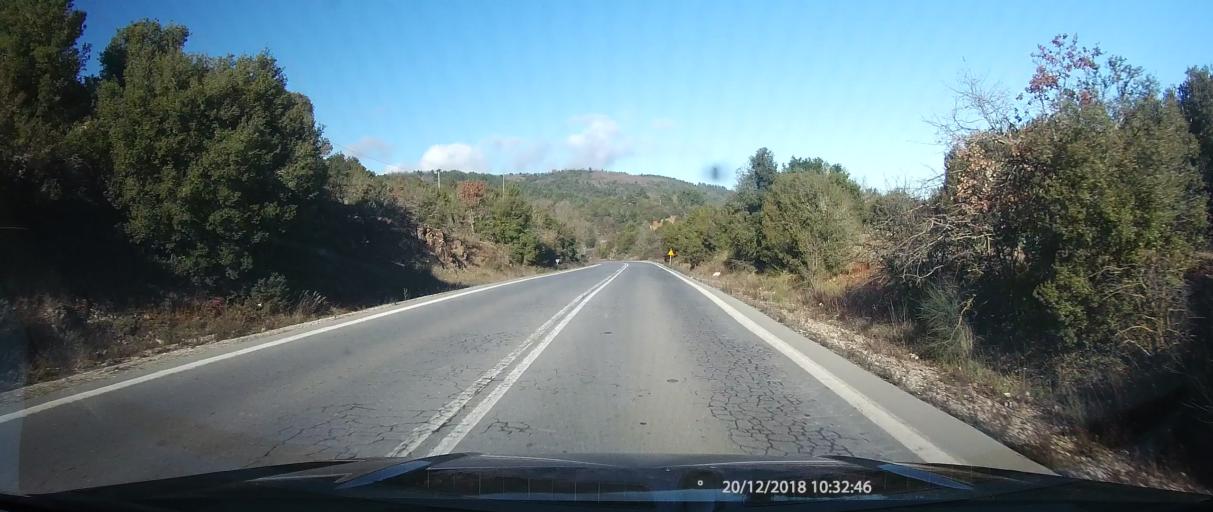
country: GR
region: Peloponnese
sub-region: Nomos Lakonias
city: Kariai
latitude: 37.3306
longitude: 22.4210
